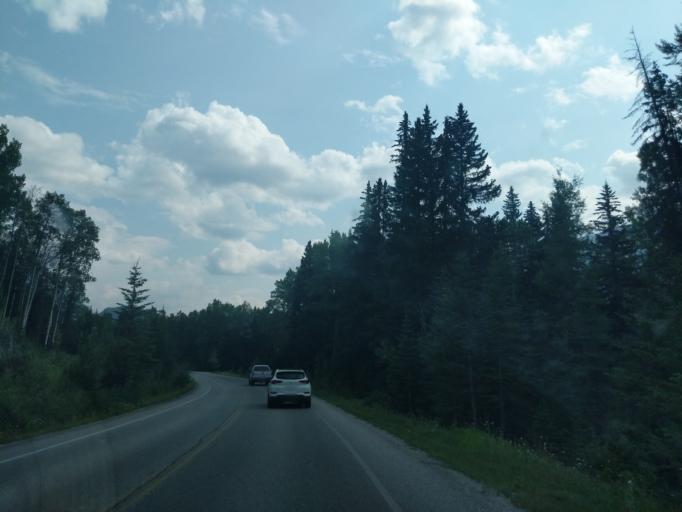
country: CA
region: Alberta
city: Banff
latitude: 51.1825
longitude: -115.7240
